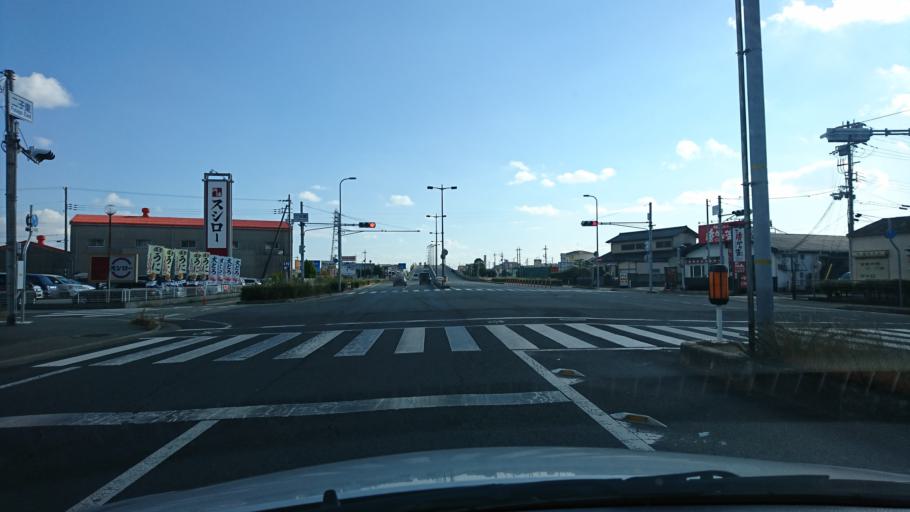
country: JP
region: Hyogo
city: Kakogawacho-honmachi
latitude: 34.7126
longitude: 134.8798
